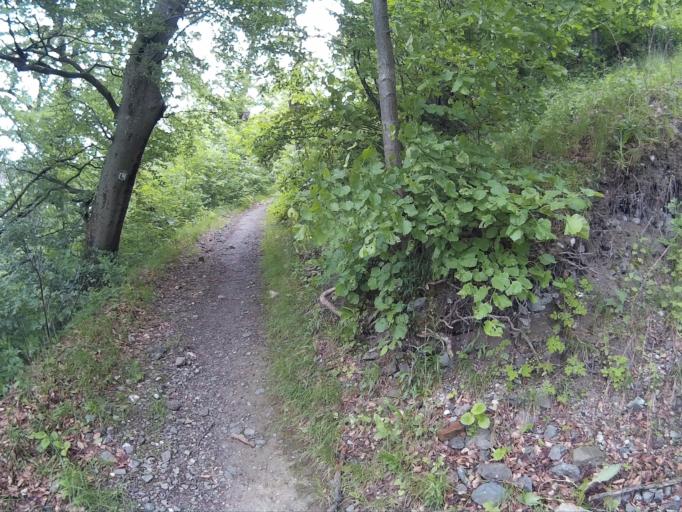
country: HU
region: Veszprem
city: Sumeg
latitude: 46.9062
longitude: 17.2594
